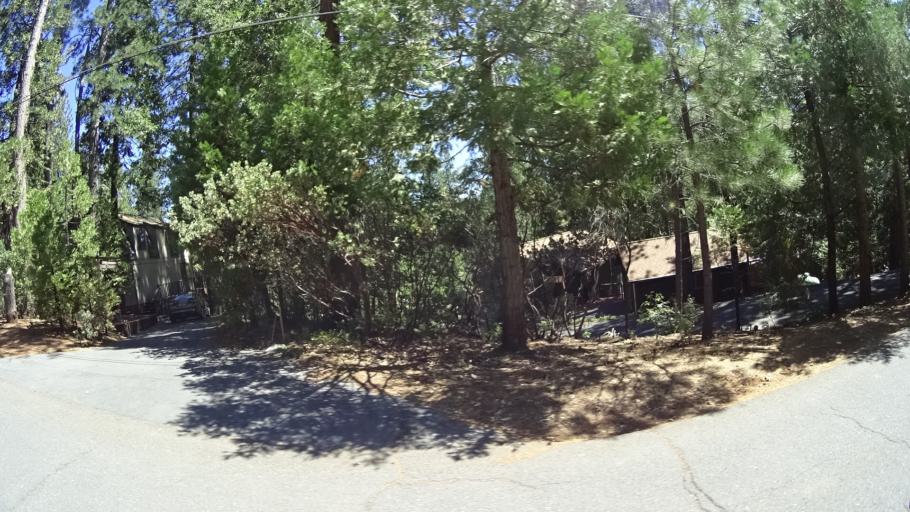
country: US
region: California
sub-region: Calaveras County
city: Arnold
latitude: 38.2306
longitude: -120.3392
